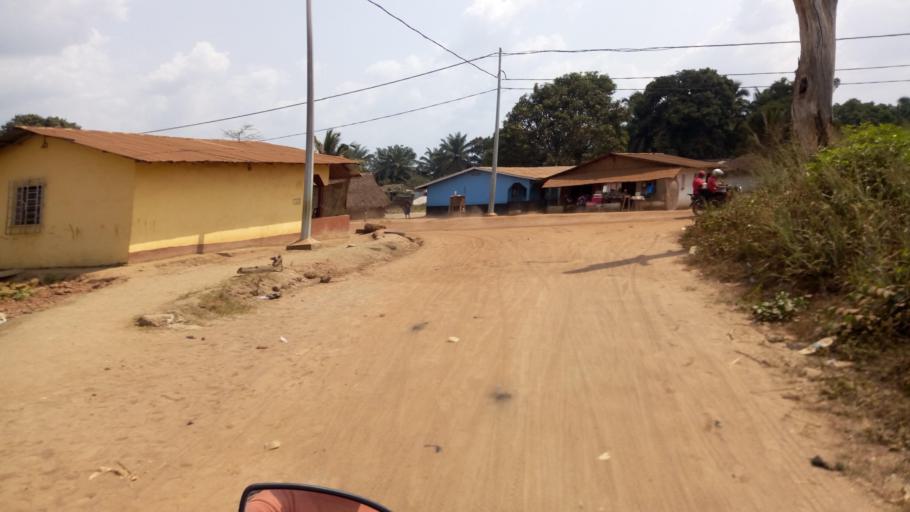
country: SL
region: Southern Province
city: Mogbwemo
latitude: 7.7897
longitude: -12.3025
